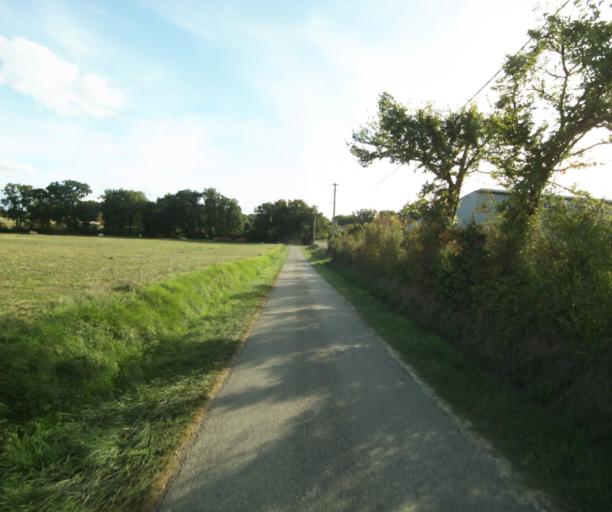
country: FR
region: Midi-Pyrenees
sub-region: Departement du Gers
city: Gondrin
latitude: 43.9101
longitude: 0.2454
